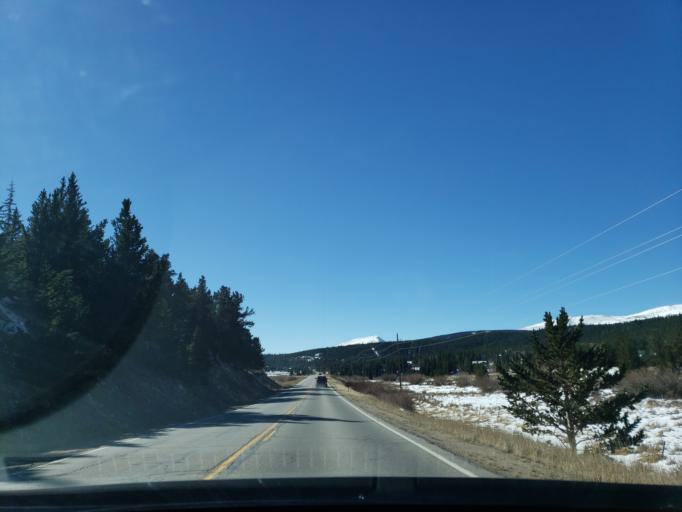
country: US
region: Colorado
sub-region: Park County
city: Fairplay
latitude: 39.3016
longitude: -106.0636
